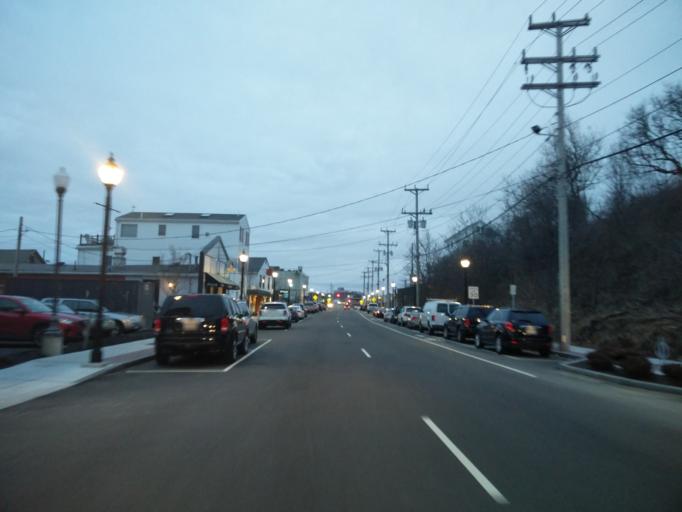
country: US
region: Massachusetts
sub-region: Plymouth County
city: Hingham
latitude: 42.2743
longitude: -70.8614
